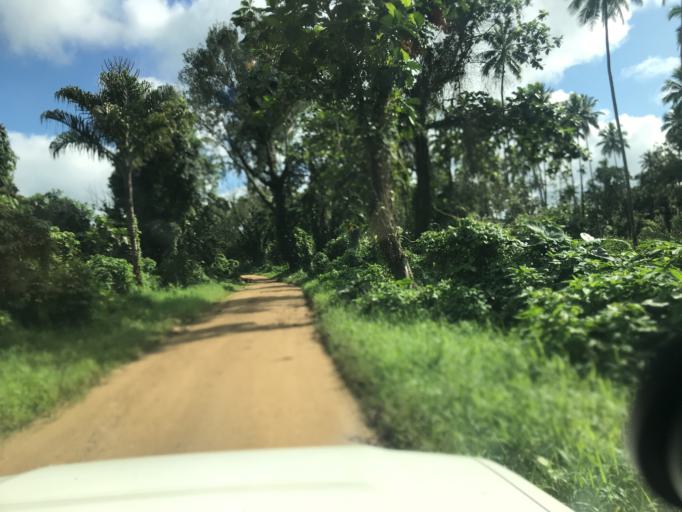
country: VU
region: Sanma
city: Luganville
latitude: -15.4760
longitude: 167.0859
